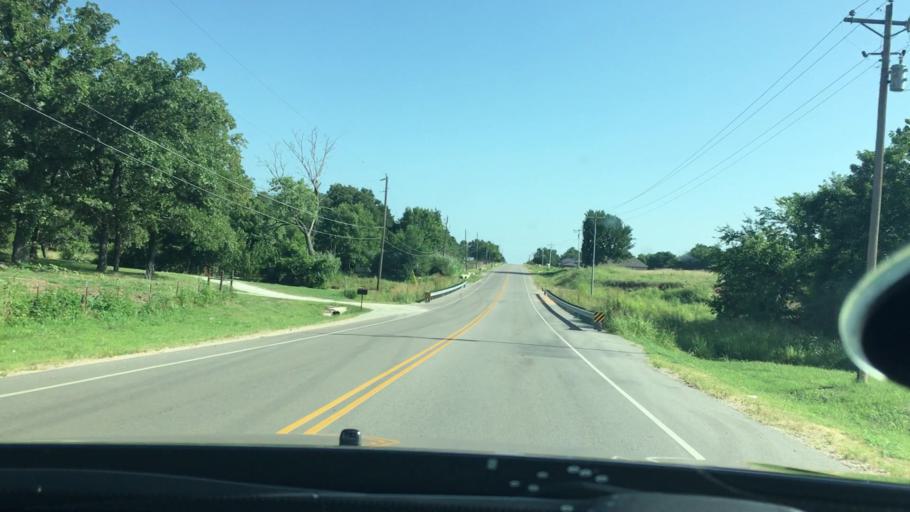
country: US
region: Oklahoma
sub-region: Pontotoc County
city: Ada
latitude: 34.8041
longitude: -96.6523
